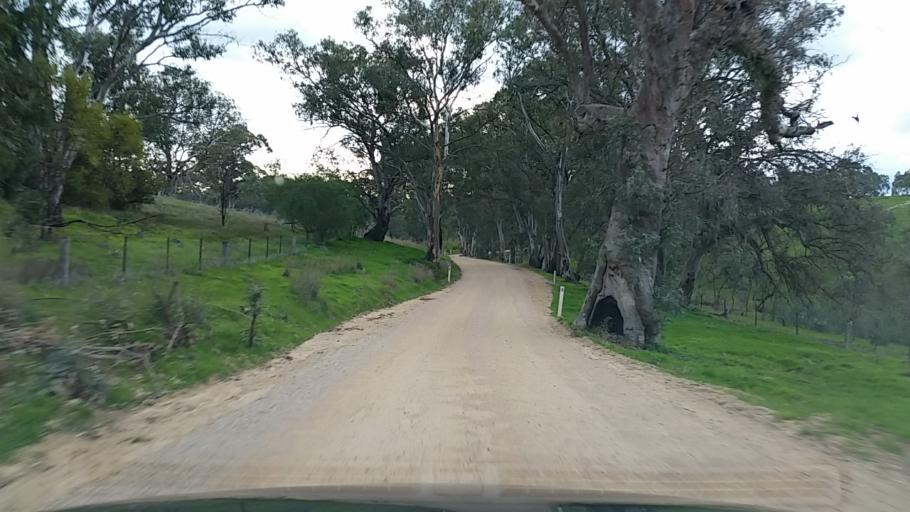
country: AU
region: South Australia
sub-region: Mount Barker
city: Nairne
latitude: -34.9670
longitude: 139.0253
